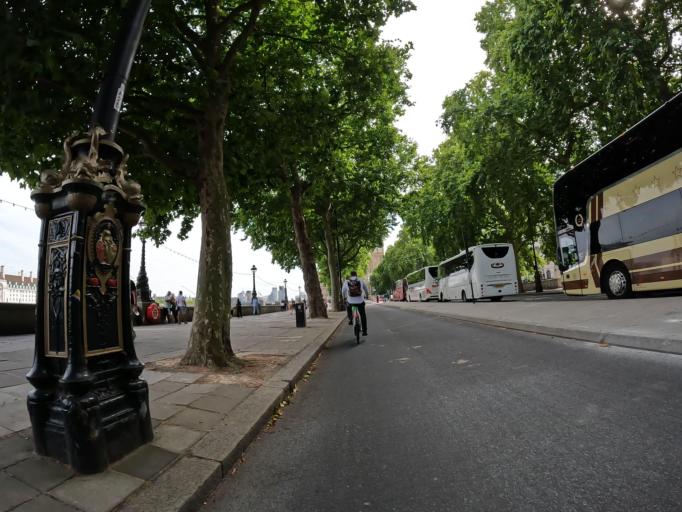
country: GB
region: England
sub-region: Greater London
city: Bromley
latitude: 51.4193
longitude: 0.0205
